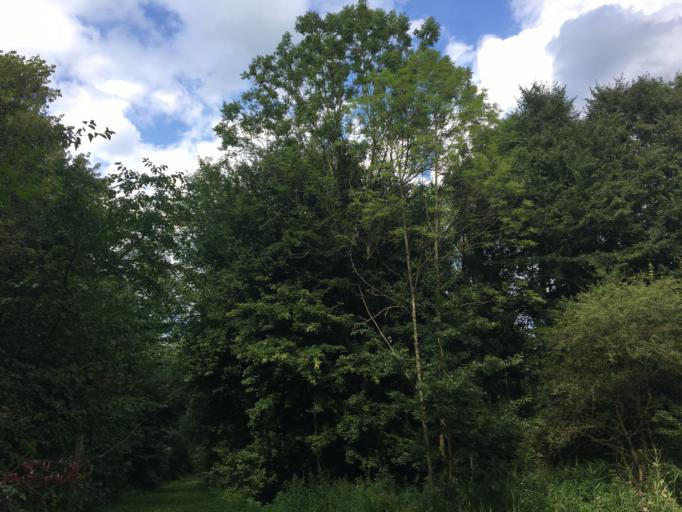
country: NL
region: Flevoland
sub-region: Gemeente Zeewolde
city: Zeewolde
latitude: 52.2810
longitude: 5.5200
